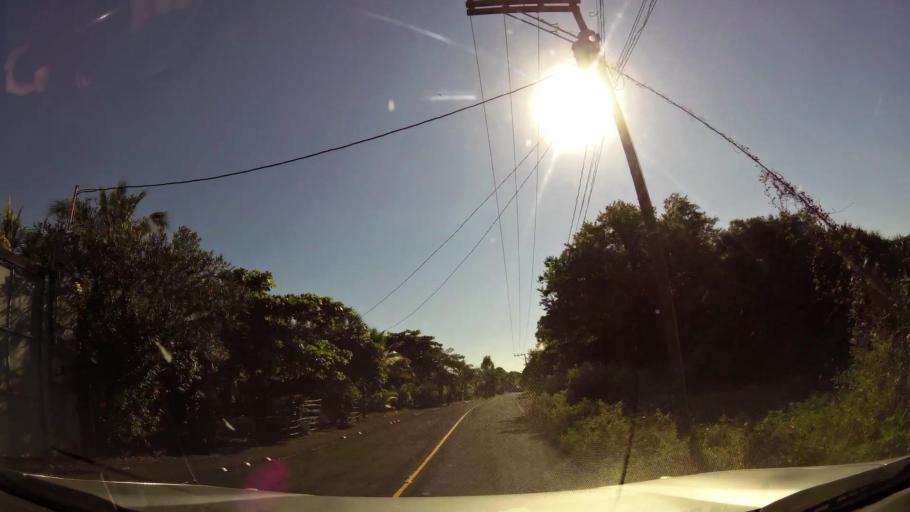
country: GT
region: Santa Rosa
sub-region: Municipio de Taxisco
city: Taxisco
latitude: 13.8860
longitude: -90.4650
